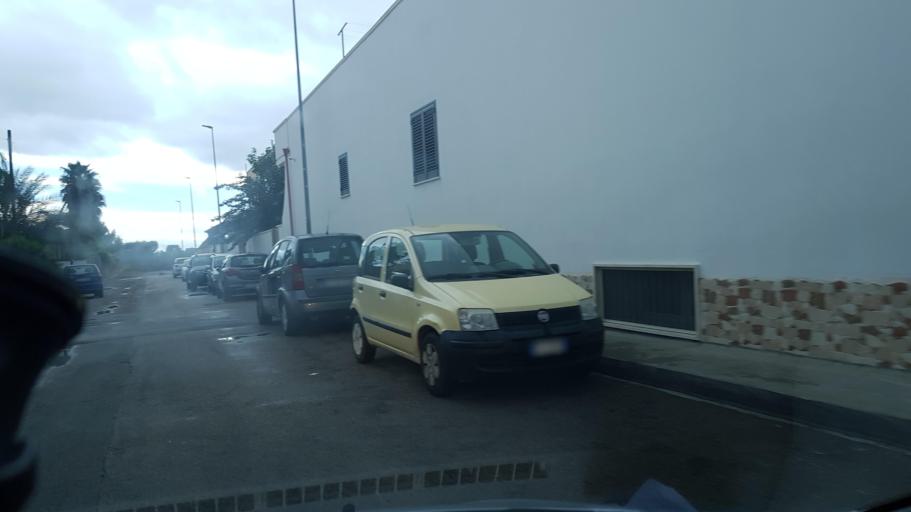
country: IT
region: Apulia
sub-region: Provincia di Lecce
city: Carmiano
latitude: 40.3501
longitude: 18.0502
